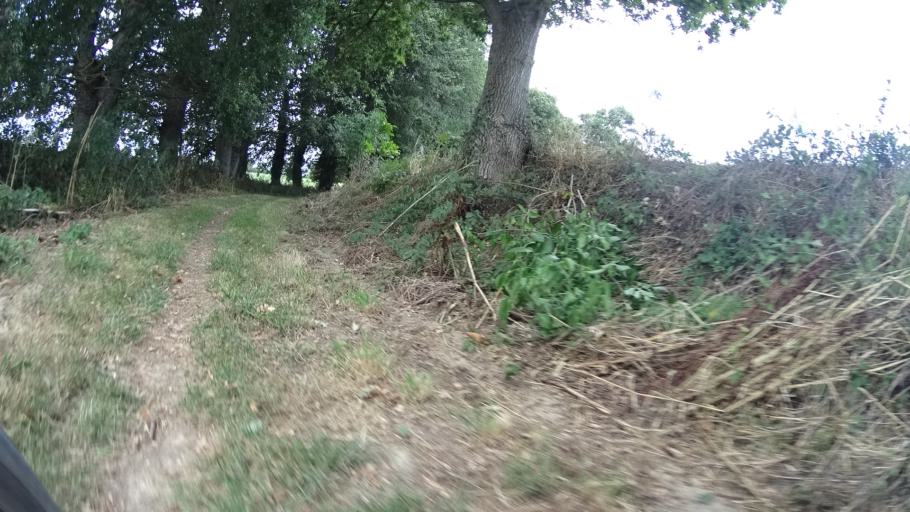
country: FR
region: Brittany
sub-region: Departement d'Ille-et-Vilaine
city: Geveze
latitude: 48.2299
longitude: -1.7817
